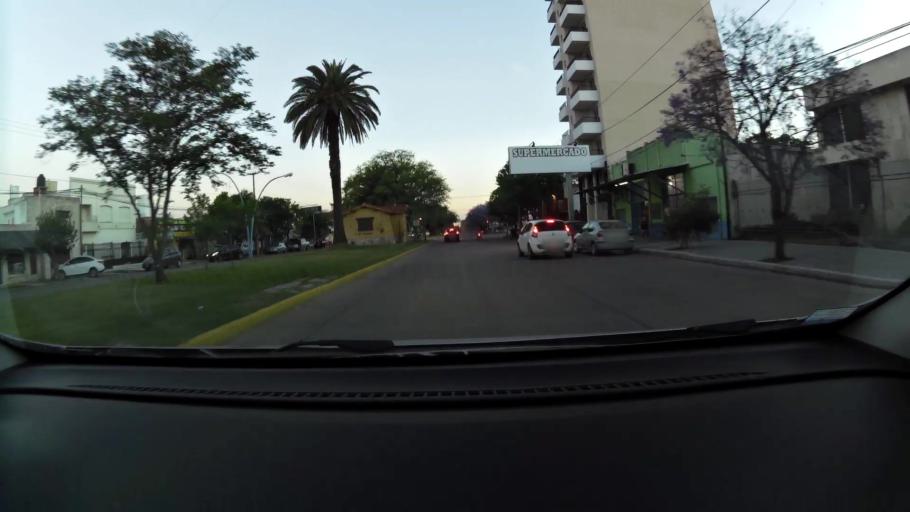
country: AR
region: Cordoba
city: Villa Maria
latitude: -32.4162
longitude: -63.2506
